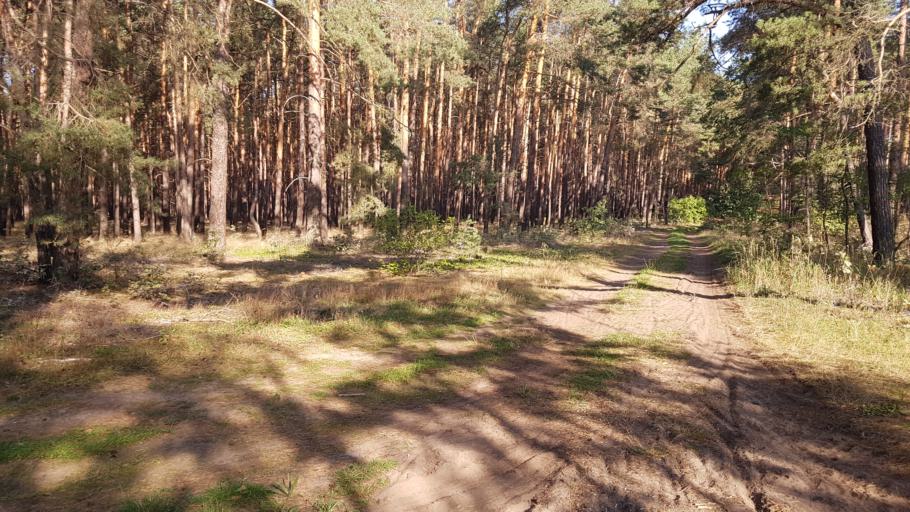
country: DE
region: Brandenburg
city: Finsterwalde
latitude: 51.6476
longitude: 13.6784
